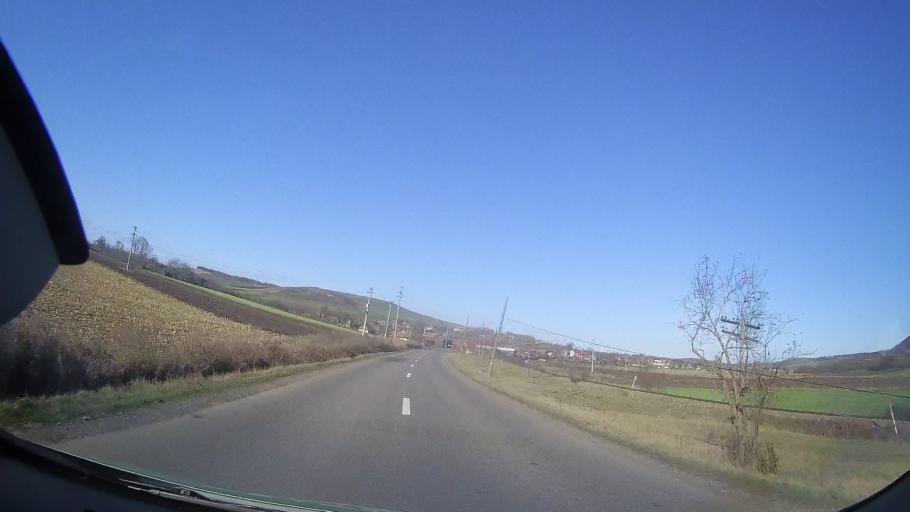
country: RO
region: Mures
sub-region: Comuna Sarmasu
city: Balda
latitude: 46.7211
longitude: 24.1446
